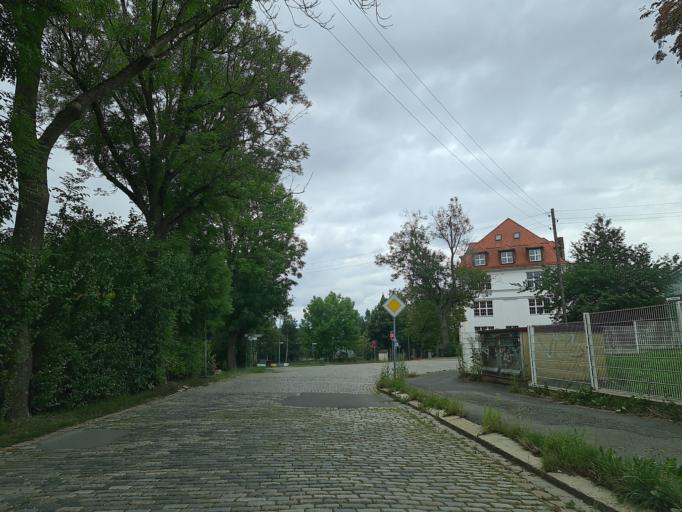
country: DE
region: Saxony
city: Plauen
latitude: 50.5184
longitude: 12.1243
